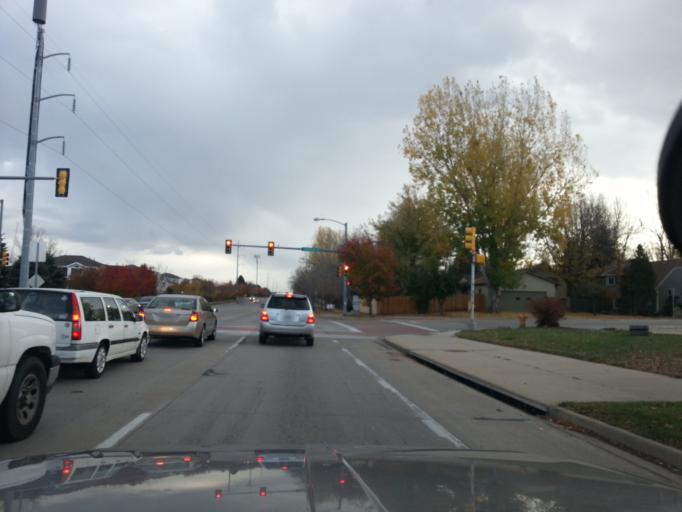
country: US
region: Colorado
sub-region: Larimer County
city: Fort Collins
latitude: 40.5527
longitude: -105.1056
